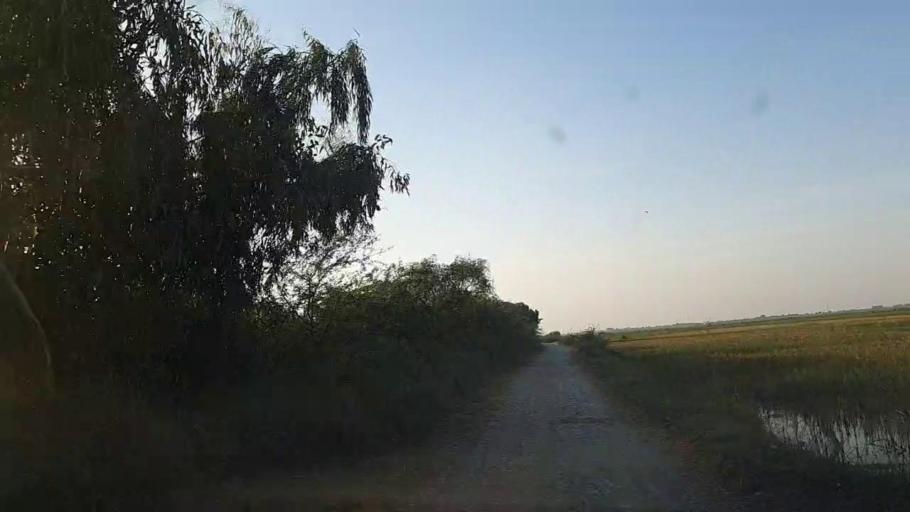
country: PK
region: Sindh
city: Mirpur Batoro
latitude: 24.6824
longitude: 68.2126
